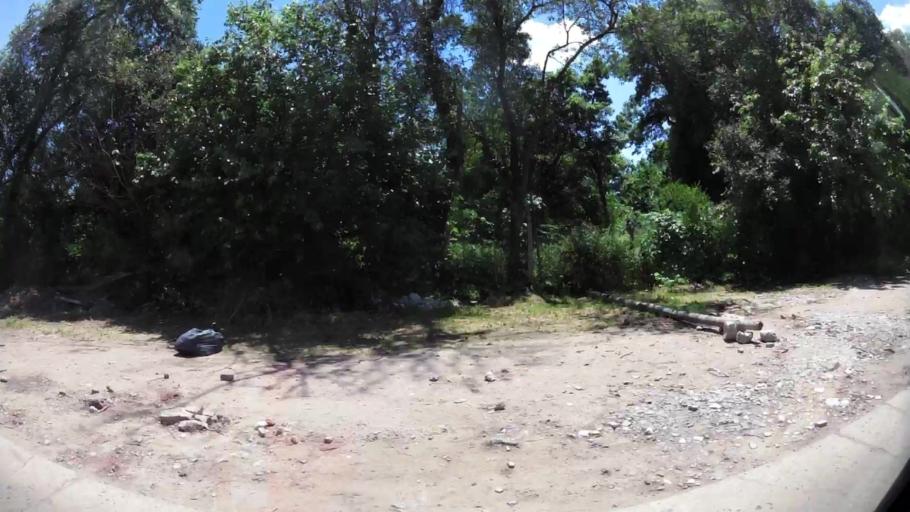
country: AR
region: Buenos Aires
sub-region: Partido de Merlo
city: Merlo
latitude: -34.6619
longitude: -58.6996
